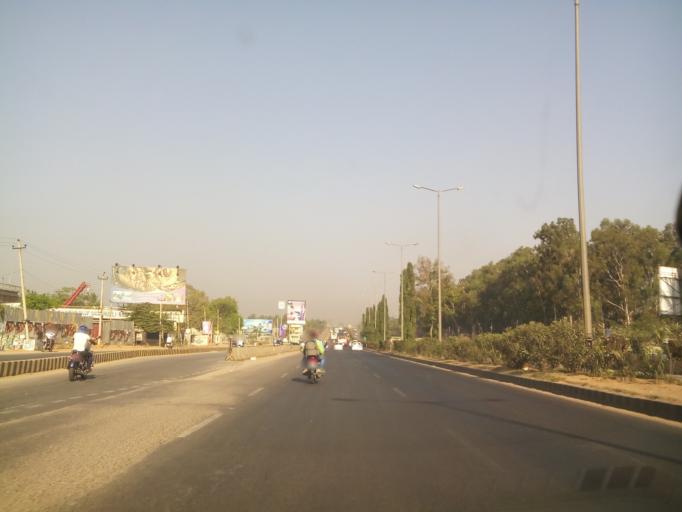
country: IN
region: Karnataka
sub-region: Bangalore Rural
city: Nelamangala
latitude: 13.0510
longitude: 77.4908
